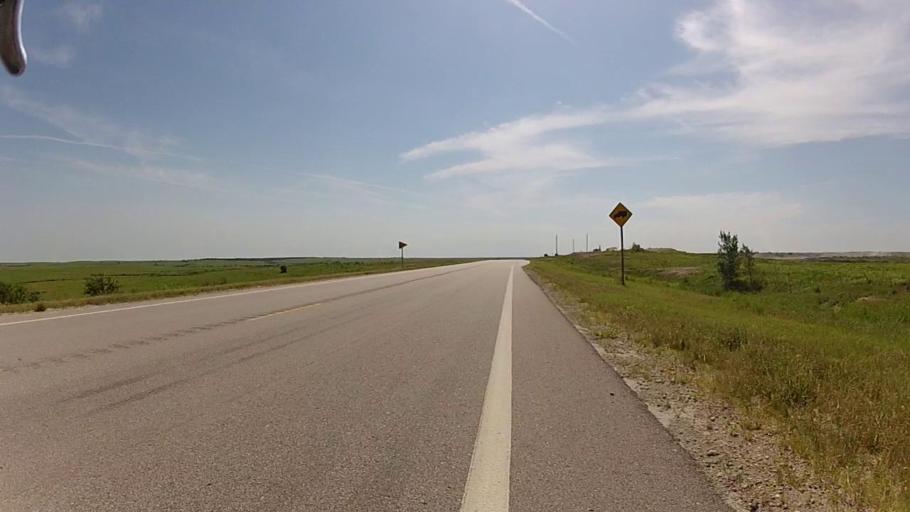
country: US
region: Kansas
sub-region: Cowley County
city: Winfield
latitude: 37.1111
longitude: -96.6088
